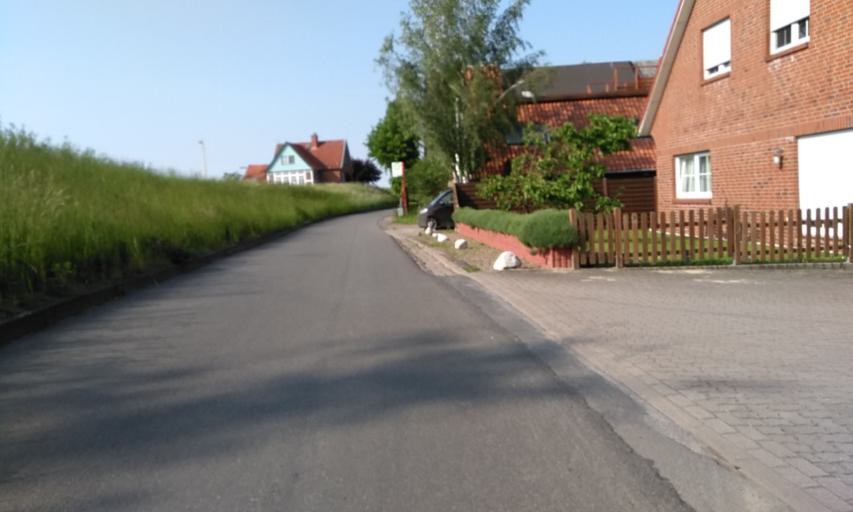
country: DE
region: Lower Saxony
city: Buxtehude
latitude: 53.4991
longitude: 9.7268
